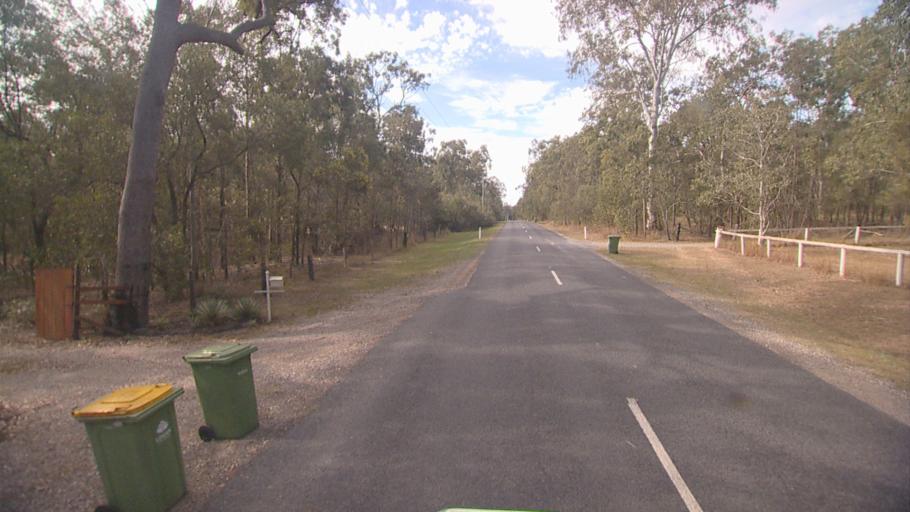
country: AU
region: Queensland
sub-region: Logan
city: North Maclean
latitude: -27.7612
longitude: 152.9762
